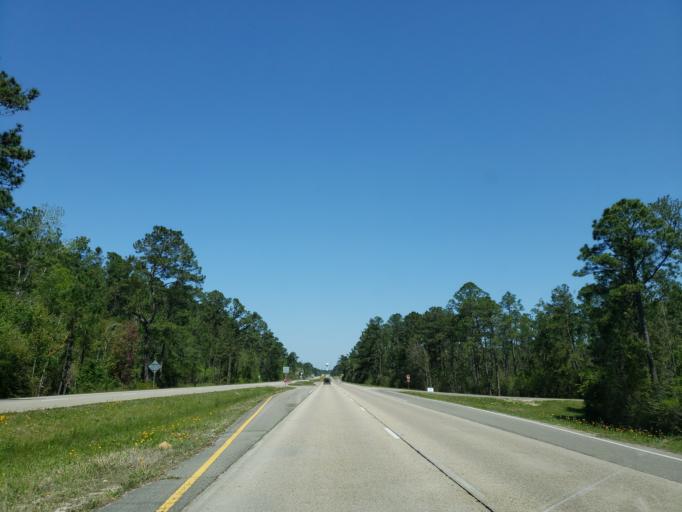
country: US
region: Mississippi
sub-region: Harrison County
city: Lyman
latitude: 30.5615
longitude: -89.1225
